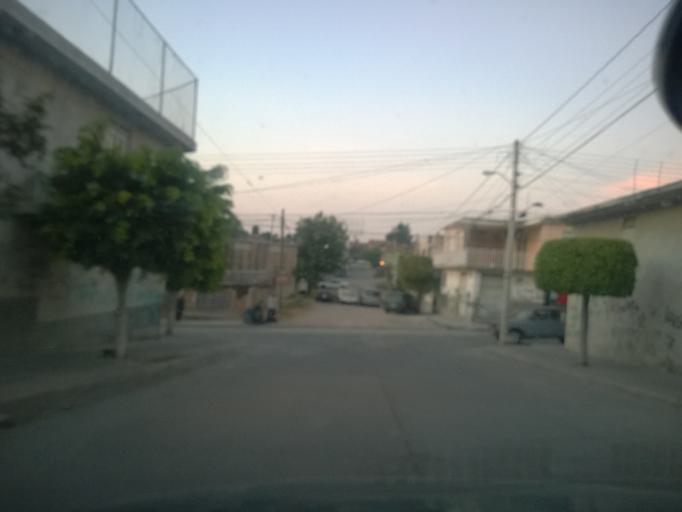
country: MX
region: Guanajuato
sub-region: Leon
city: Ejido la Joya
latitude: 21.1260
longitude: -101.7126
